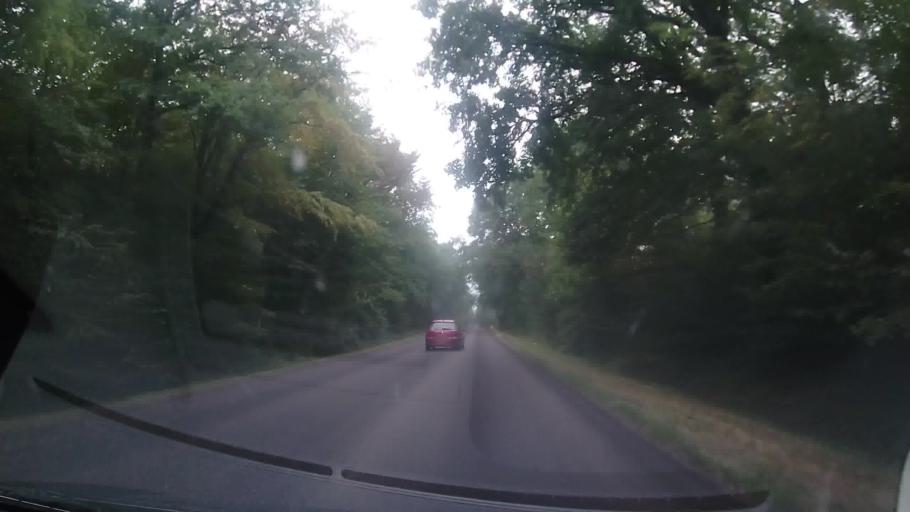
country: FR
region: Ile-de-France
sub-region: Departement de l'Essonne
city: Dourdan
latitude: 48.5438
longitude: 1.9933
